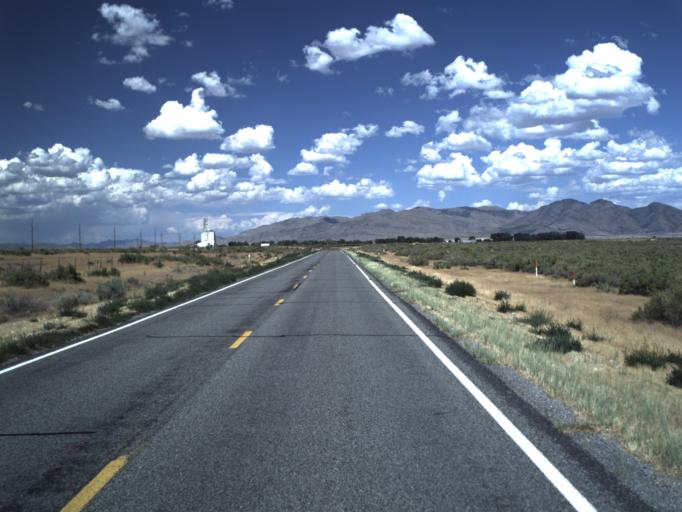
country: US
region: Utah
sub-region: Millard County
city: Delta
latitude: 39.5014
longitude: -112.3911
